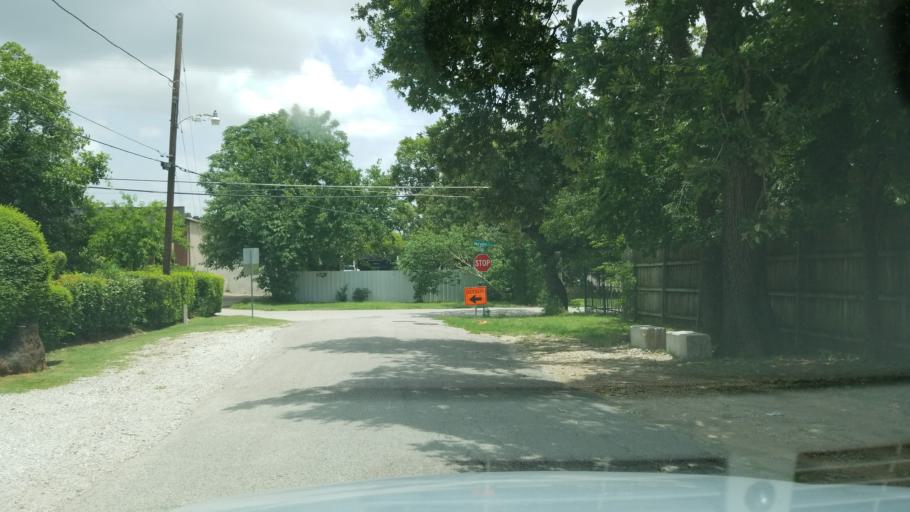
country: US
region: Texas
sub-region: Dallas County
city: Irving
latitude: 32.8287
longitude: -96.9081
